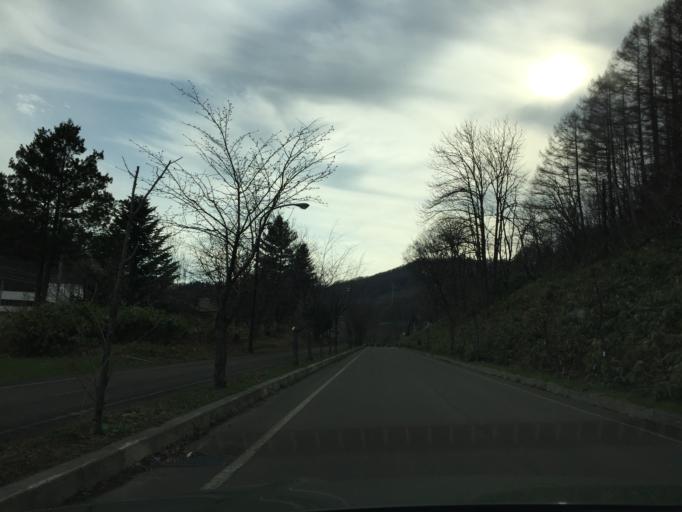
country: JP
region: Hokkaido
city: Utashinai
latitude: 43.5227
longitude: 142.0361
